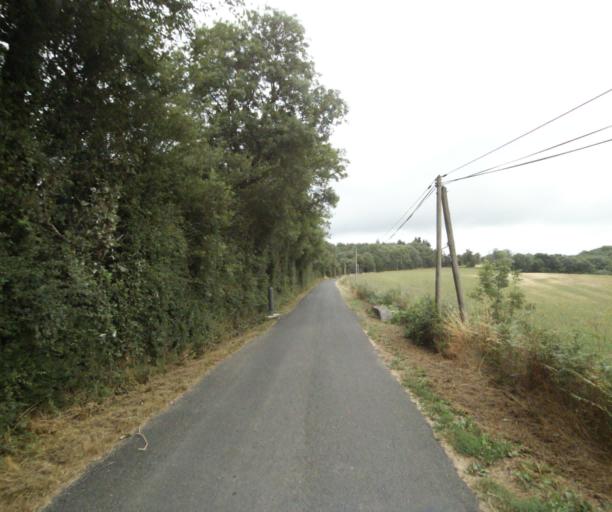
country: FR
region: Midi-Pyrenees
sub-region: Departement du Tarn
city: Soreze
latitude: 43.3989
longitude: 2.0580
